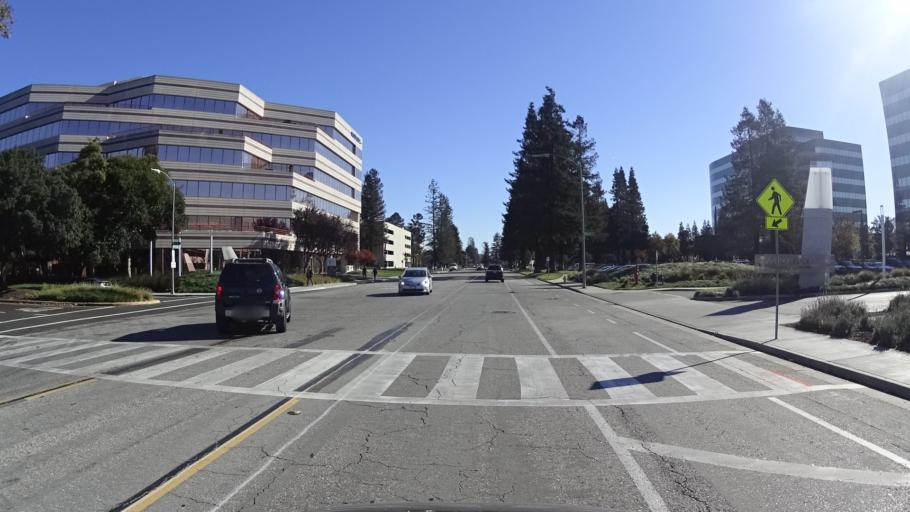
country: US
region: California
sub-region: Santa Clara County
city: San Jose
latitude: 37.3680
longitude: -121.9191
